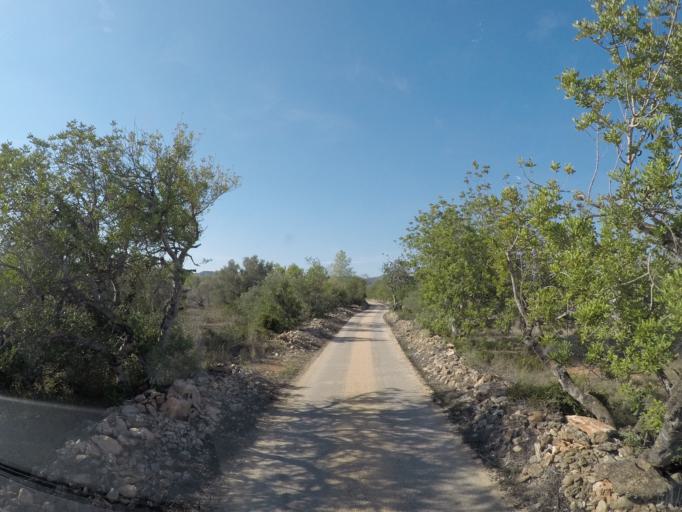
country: ES
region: Catalonia
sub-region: Provincia de Tarragona
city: El Perello
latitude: 40.9003
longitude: 0.7311
